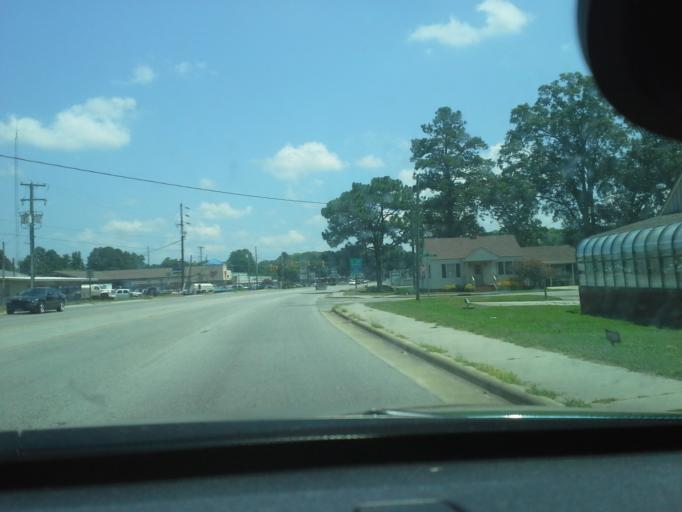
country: US
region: North Carolina
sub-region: Washington County
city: Plymouth
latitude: 35.8577
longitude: -76.7470
